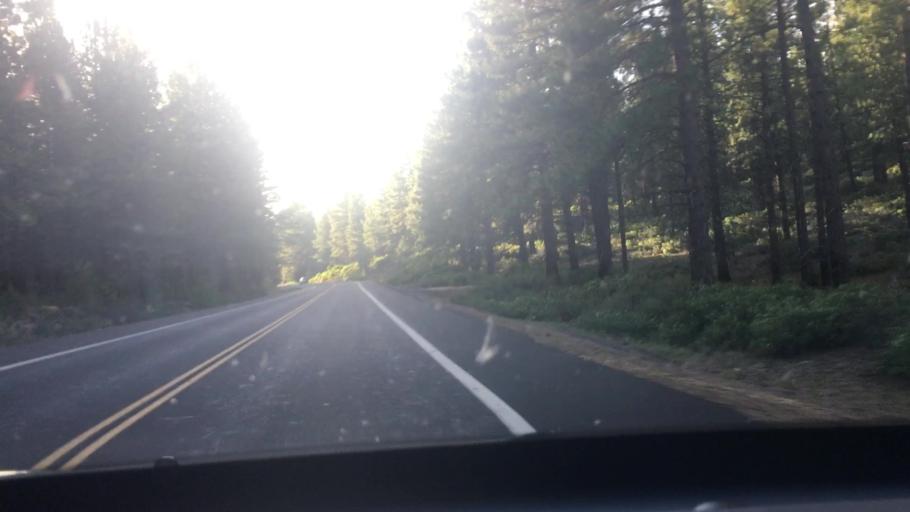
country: US
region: Oregon
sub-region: Deschutes County
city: Deschutes River Woods
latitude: 44.0383
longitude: -121.4618
